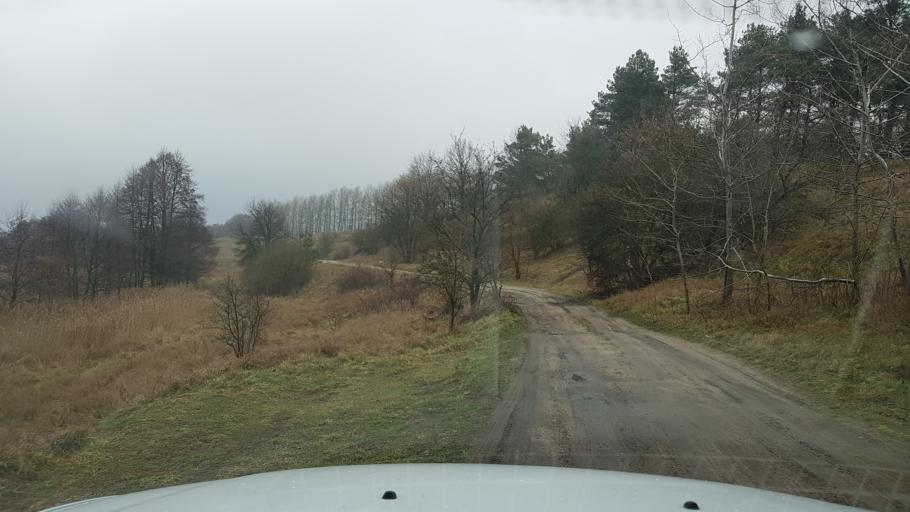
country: PL
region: West Pomeranian Voivodeship
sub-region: Powiat drawski
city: Czaplinek
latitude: 53.5642
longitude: 16.2466
